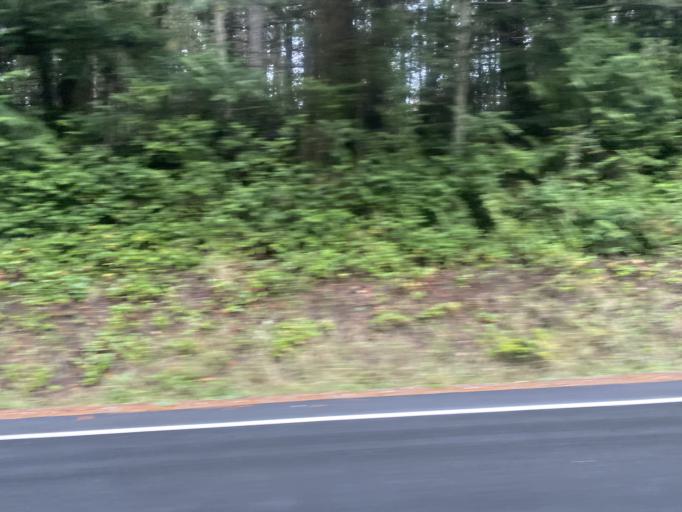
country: US
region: Washington
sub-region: Island County
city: Freeland
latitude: 48.0765
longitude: -122.4851
